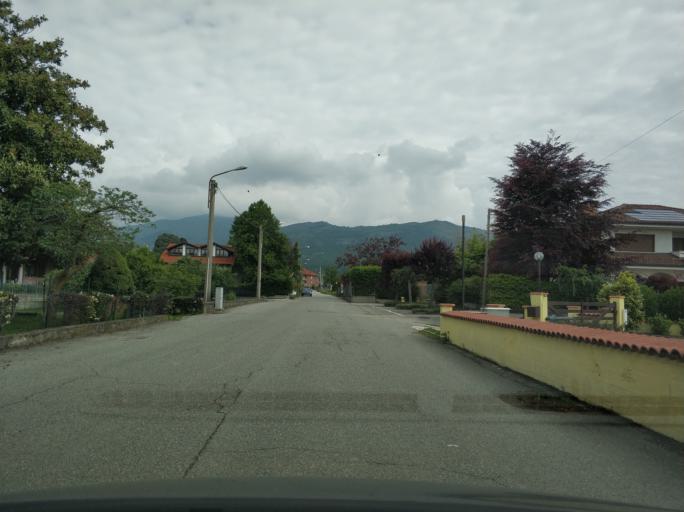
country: IT
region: Piedmont
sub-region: Provincia di Torino
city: Balangero
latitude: 45.2627
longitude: 7.5227
